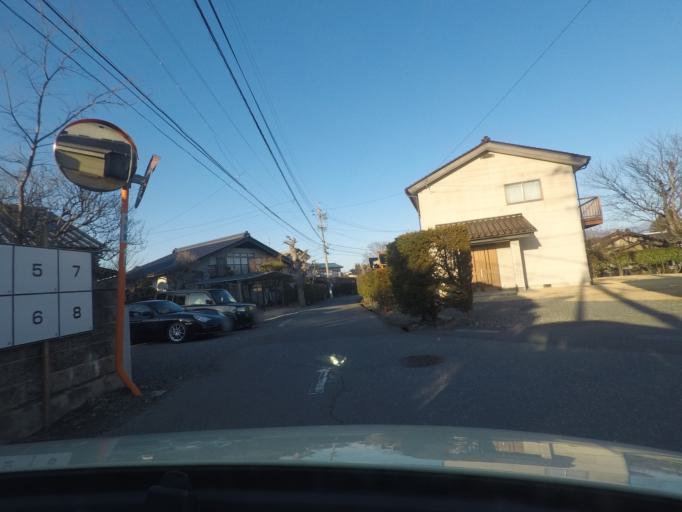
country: JP
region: Nagano
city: Matsumoto
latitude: 36.2136
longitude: 137.8902
